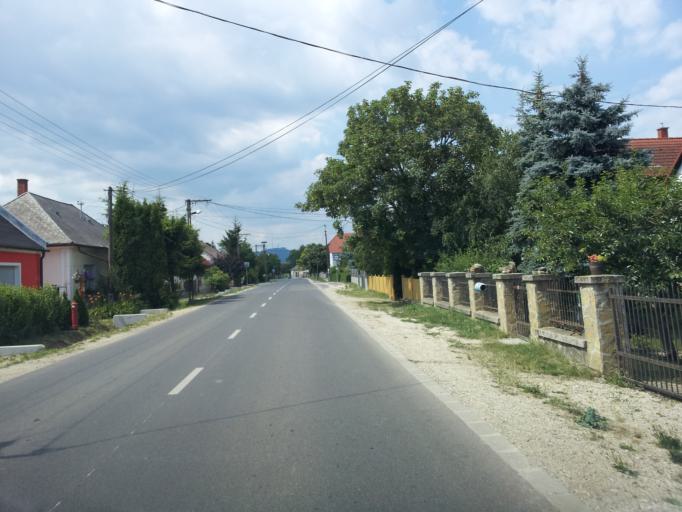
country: HU
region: Veszprem
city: Zanka
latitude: 46.9785
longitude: 17.7037
